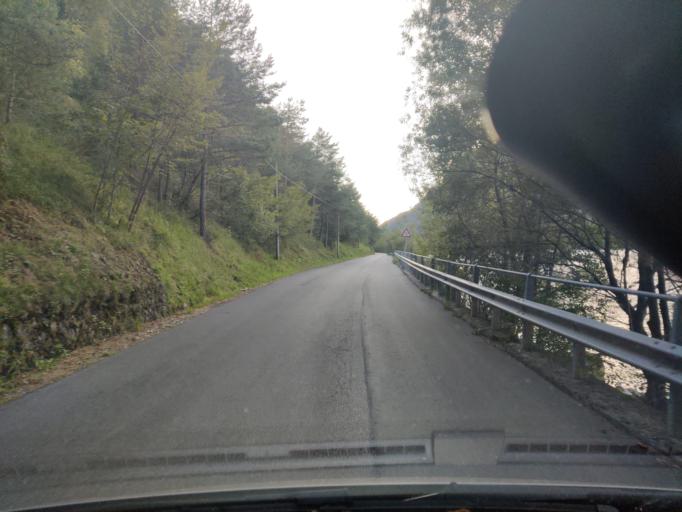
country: IT
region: Lombardy
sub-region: Provincia di Brescia
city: Anfo
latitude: 45.7577
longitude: 10.5056
